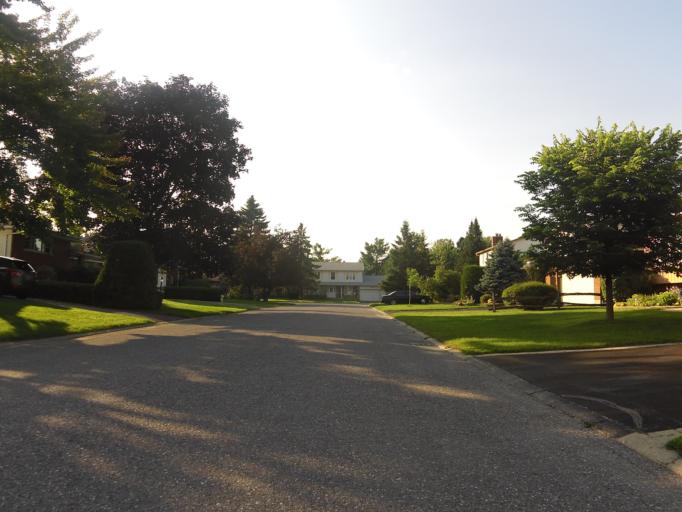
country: CA
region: Ontario
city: Bells Corners
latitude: 45.3307
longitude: -75.7915
